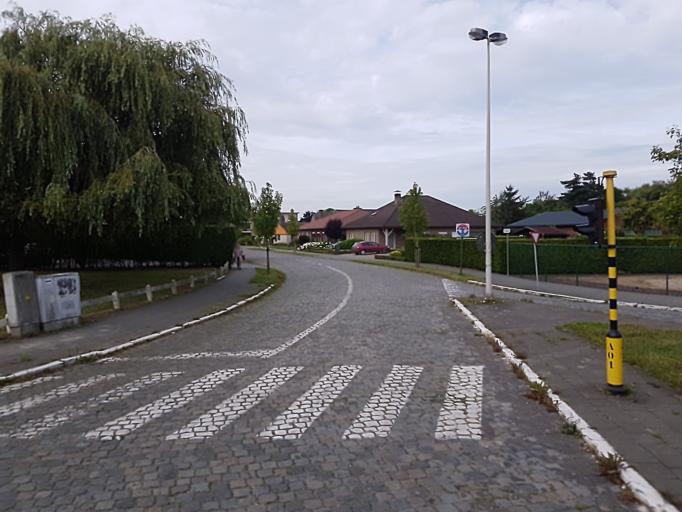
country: BE
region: Flanders
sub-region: Provincie Antwerpen
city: Ranst
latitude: 51.1892
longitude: 4.5576
